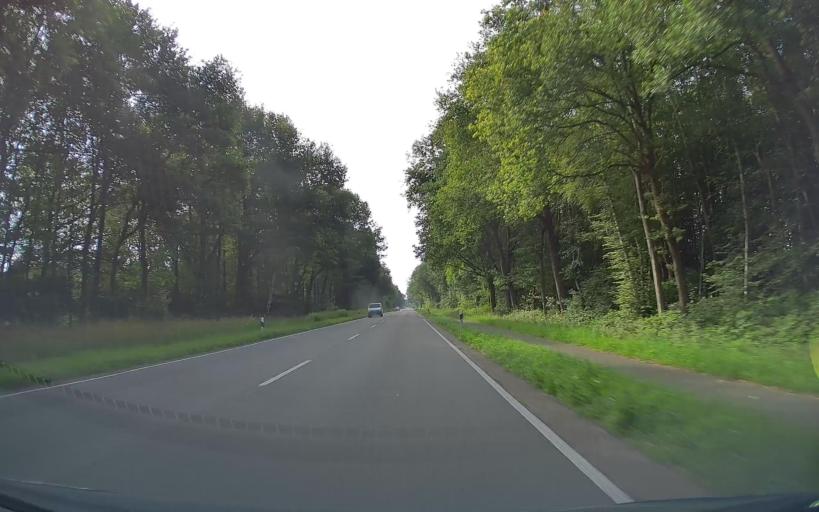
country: DE
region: Lower Saxony
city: Friesoythe
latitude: 52.9946
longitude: 7.8799
